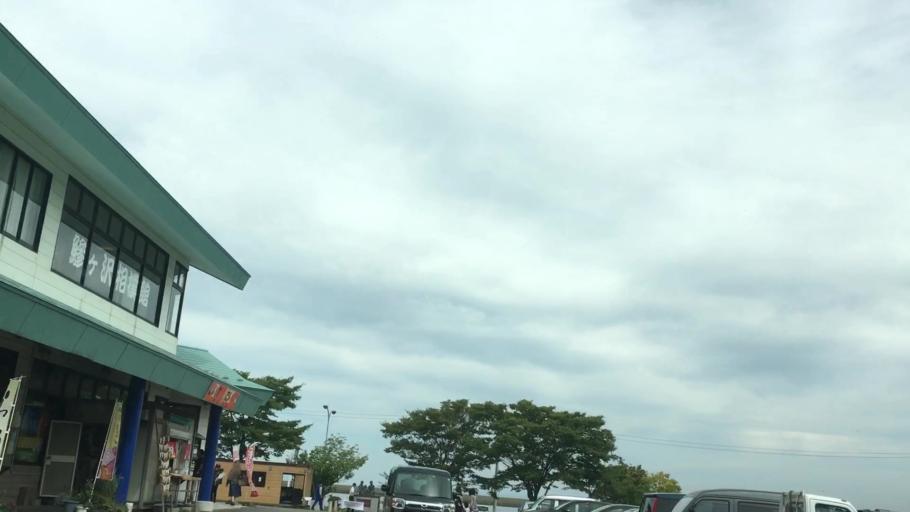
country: JP
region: Aomori
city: Shimokizukuri
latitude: 40.7790
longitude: 140.2104
